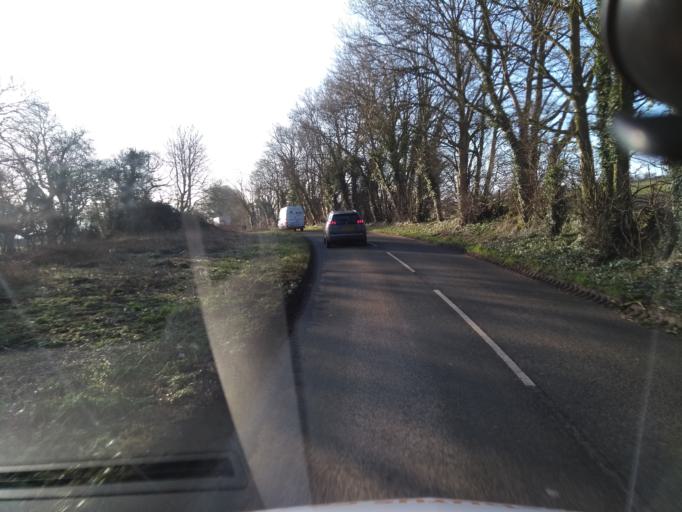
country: GB
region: England
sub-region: Somerset
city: Bruton
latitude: 51.1262
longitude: -2.4697
